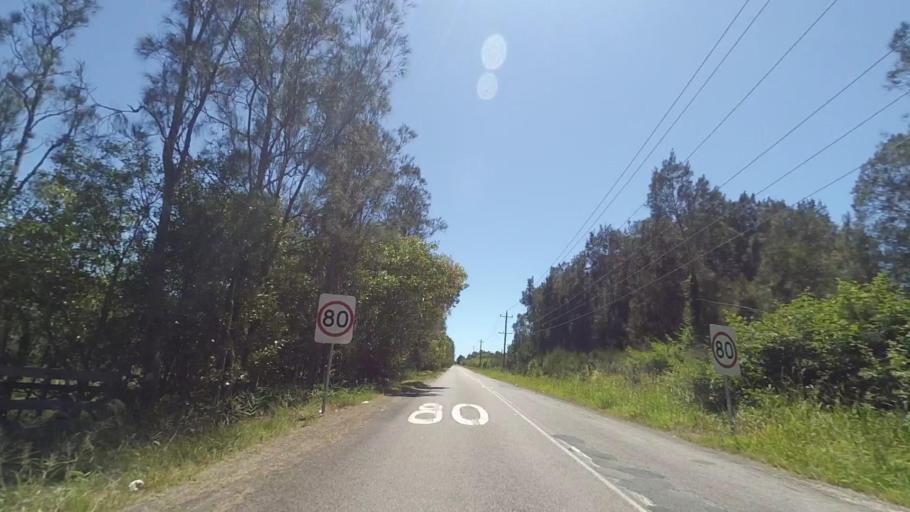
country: AU
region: New South Wales
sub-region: Port Stephens Shire
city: Medowie
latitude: -32.7867
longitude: 151.9358
